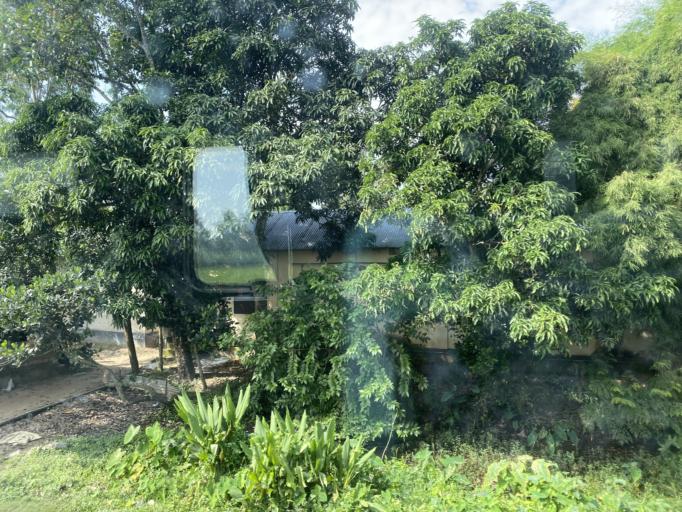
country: BD
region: Sylhet
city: Habiganj
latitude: 24.1746
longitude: 91.3579
